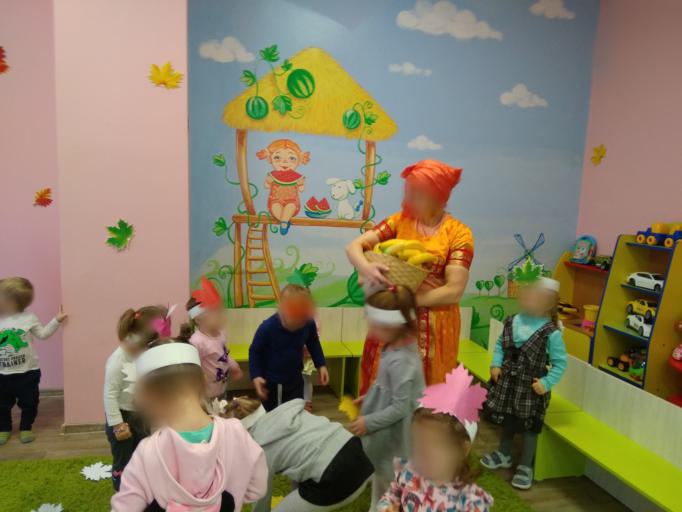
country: RU
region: Moskovskaya
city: Zheleznodorozhnyy
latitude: 55.7401
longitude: 38.0155
